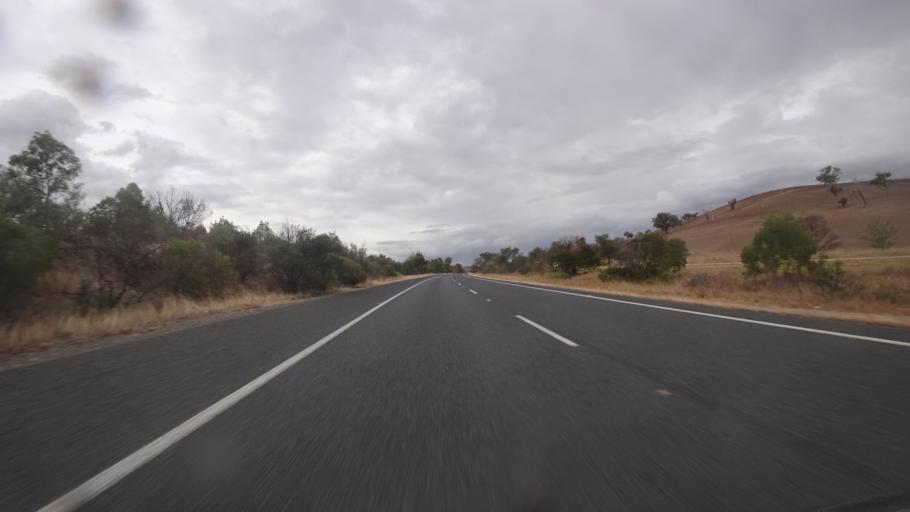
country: AU
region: New South Wales
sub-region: Yass Valley
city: Yass
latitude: -34.7899
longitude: 148.6984
